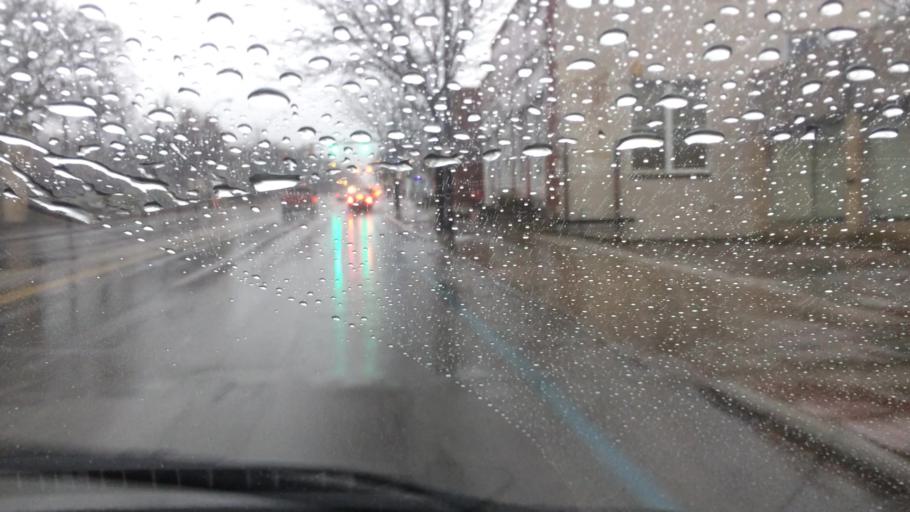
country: US
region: Ohio
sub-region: Summit County
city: Akron
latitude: 41.0928
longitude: -81.5343
